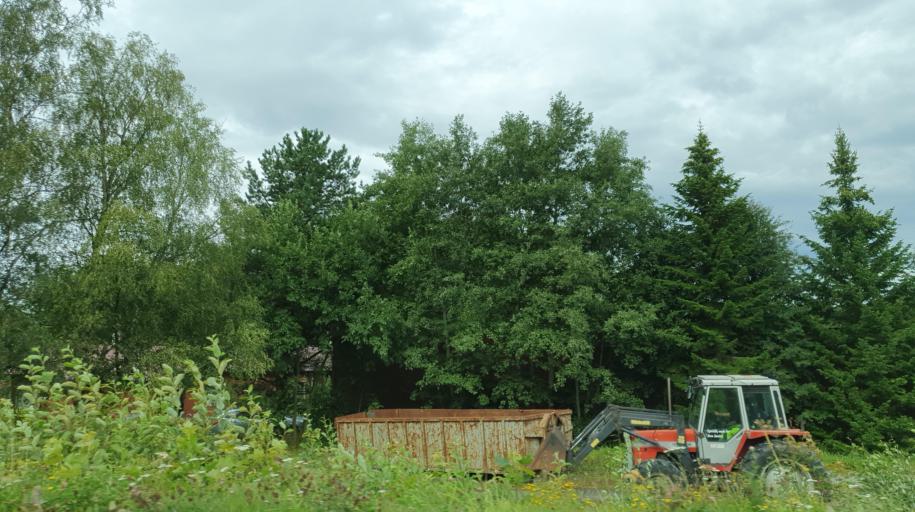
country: NO
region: Nord-Trondelag
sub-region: Stjordal
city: Stjordalshalsen
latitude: 63.4475
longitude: 10.9471
